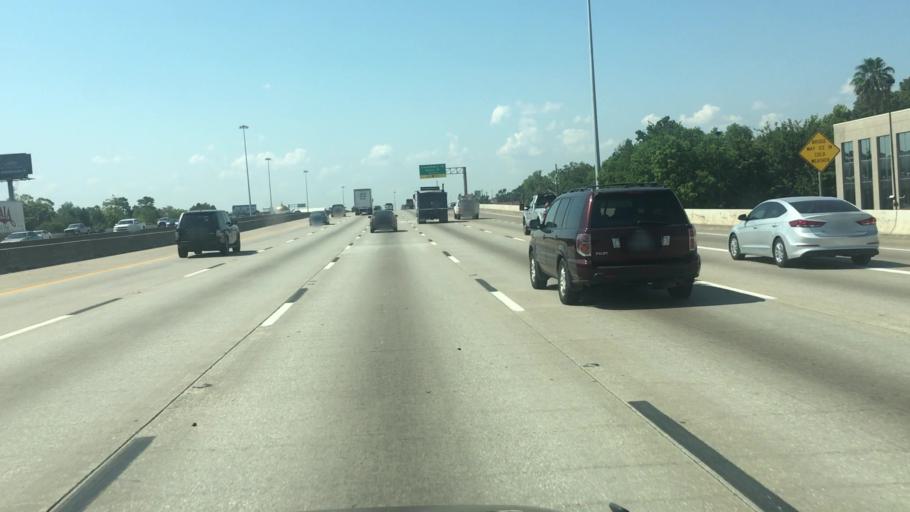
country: US
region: Texas
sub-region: Harris County
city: Houston
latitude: 29.8440
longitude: -95.3337
